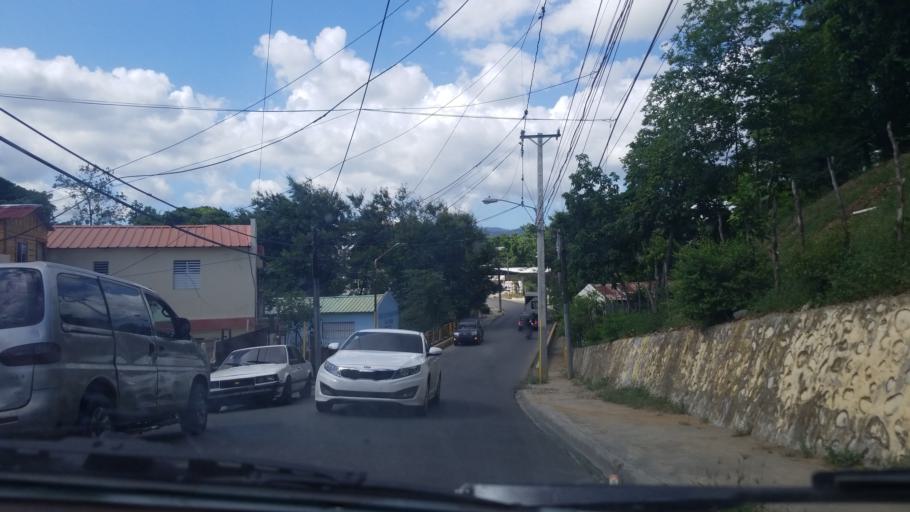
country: DO
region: Santiago
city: Santiago de los Caballeros
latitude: 19.4802
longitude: -70.6878
